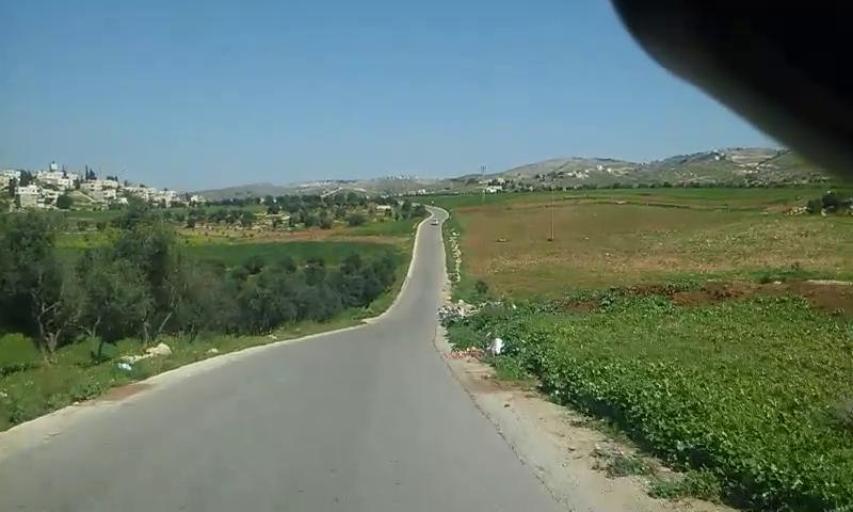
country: PS
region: West Bank
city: Dayr al `Asal al Fawqa
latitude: 31.4685
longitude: 34.9431
